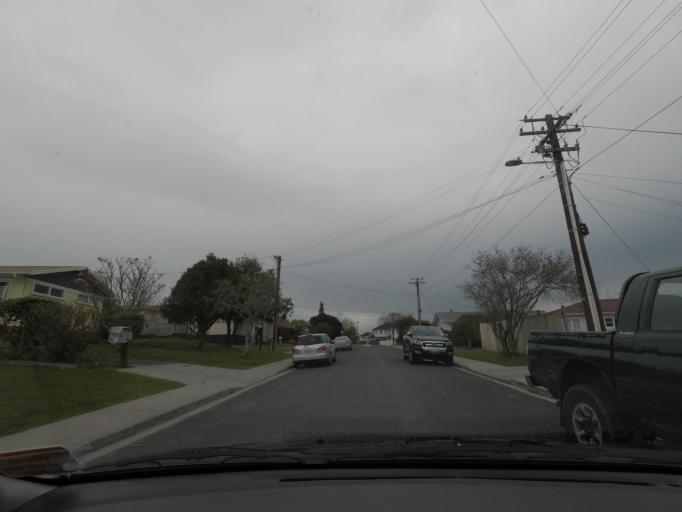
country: NZ
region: Auckland
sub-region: Auckland
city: Rosebank
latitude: -36.8578
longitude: 174.6443
